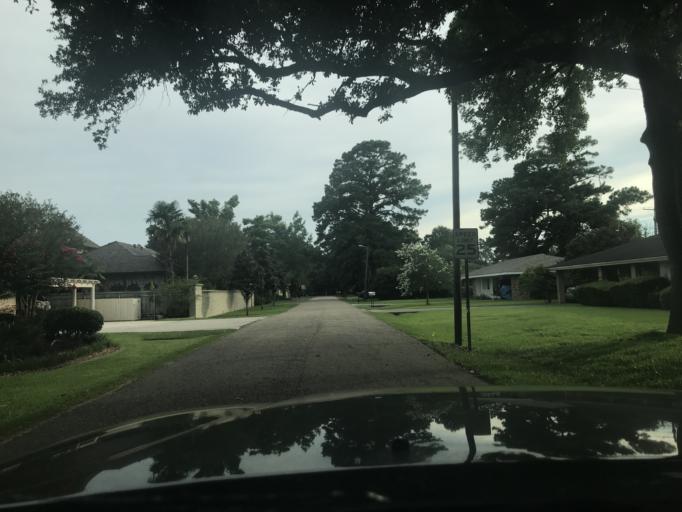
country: US
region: Louisiana
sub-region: Lafayette Parish
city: Lafayette
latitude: 30.2013
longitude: -92.0479
